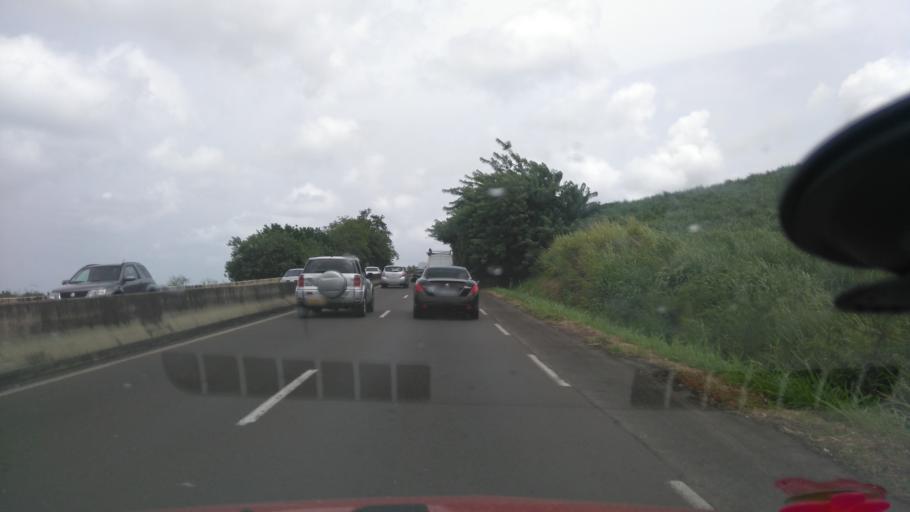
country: MQ
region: Martinique
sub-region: Martinique
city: Ducos
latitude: 14.5611
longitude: -60.9758
